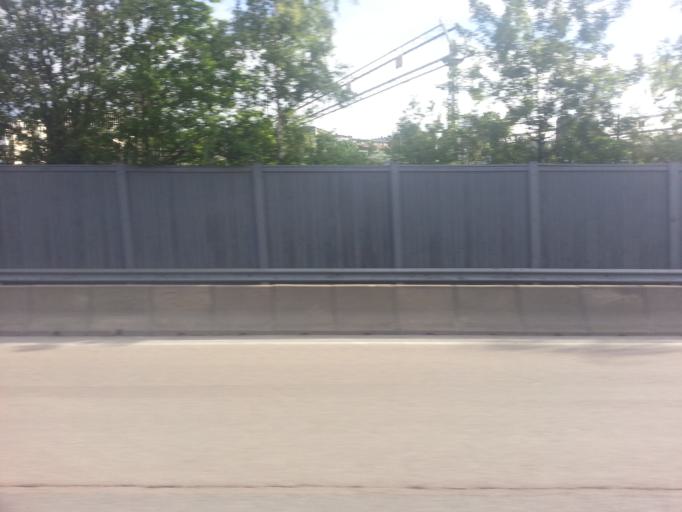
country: NO
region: Oslo
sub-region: Oslo
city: Oslo
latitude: 59.9100
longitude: 10.7134
